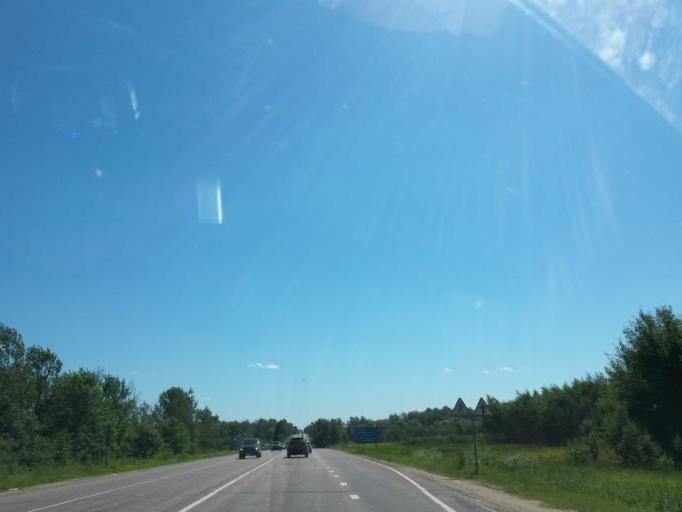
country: RU
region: Moskovskaya
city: Proletarskiy
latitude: 55.0427
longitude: 37.4309
